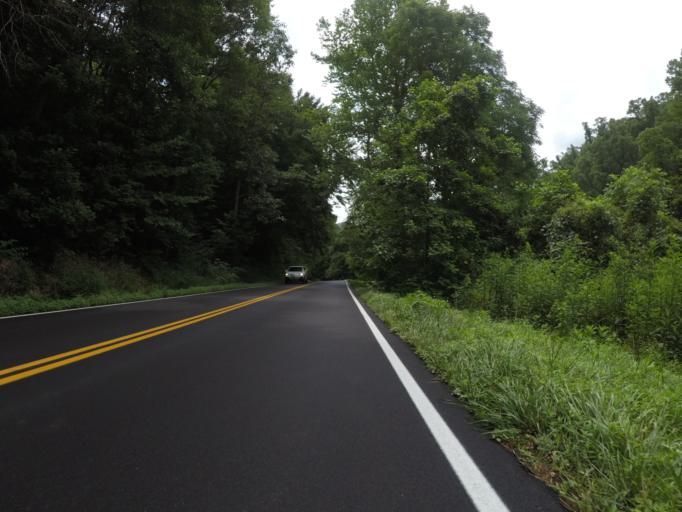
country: US
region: Kentucky
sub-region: Boyd County
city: Catlettsburg
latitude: 38.4244
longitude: -82.6273
